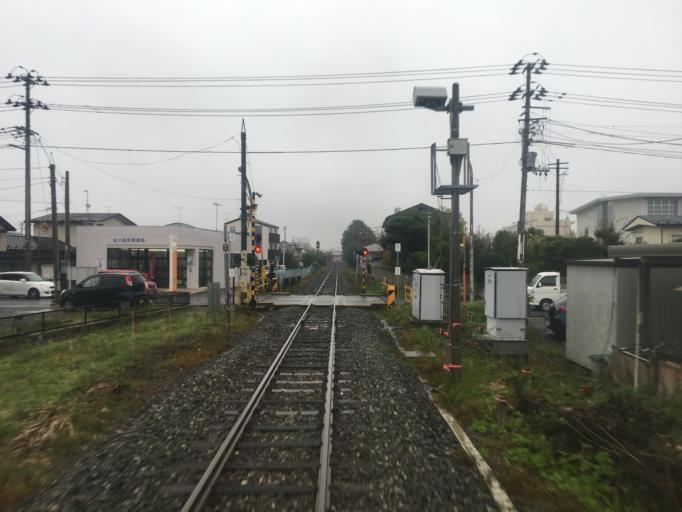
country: JP
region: Miyagi
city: Furukawa
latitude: 38.5715
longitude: 140.9543
